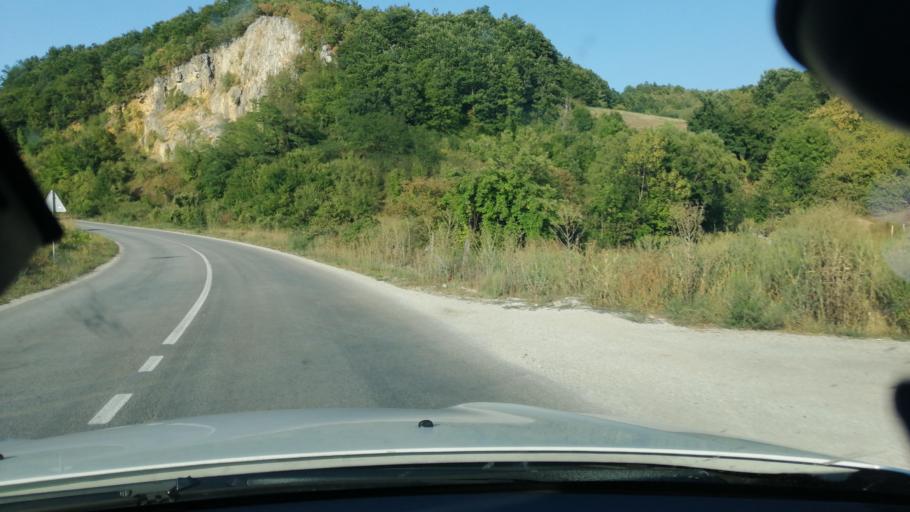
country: RS
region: Central Serbia
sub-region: Moravicki Okrug
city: Ivanjica
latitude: 43.7111
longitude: 20.2446
